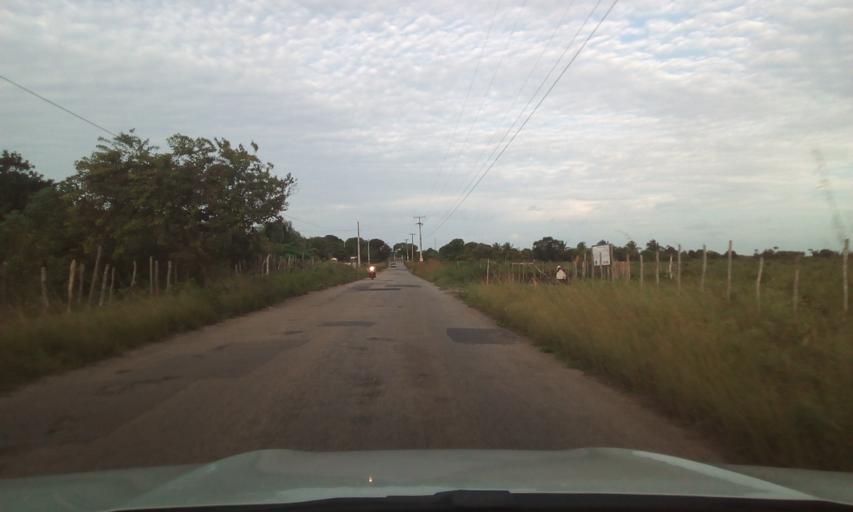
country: BR
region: Paraiba
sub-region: Conde
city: Conde
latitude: -7.2227
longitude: -34.8262
